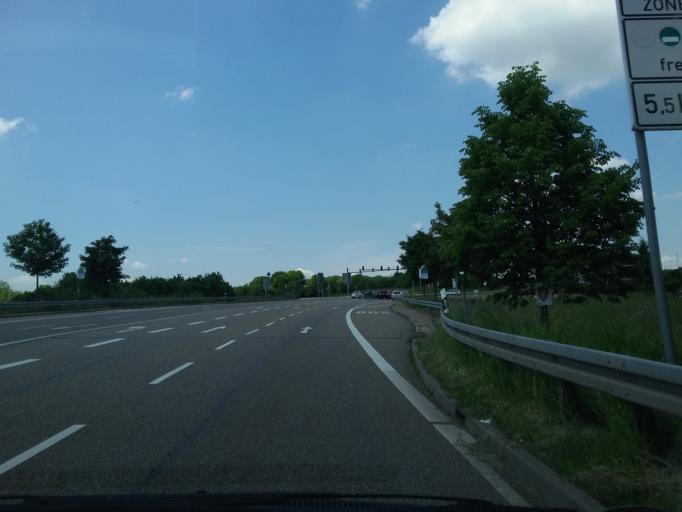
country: DE
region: Baden-Wuerttemberg
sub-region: Regierungsbezirk Stuttgart
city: Untergruppenbach
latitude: 49.0871
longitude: 9.2731
